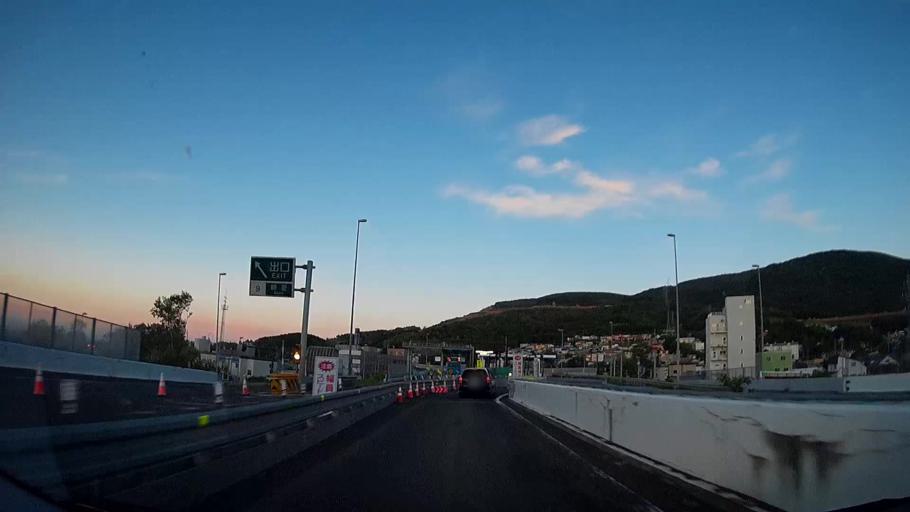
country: JP
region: Hokkaido
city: Otaru
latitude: 43.1683
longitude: 141.0459
